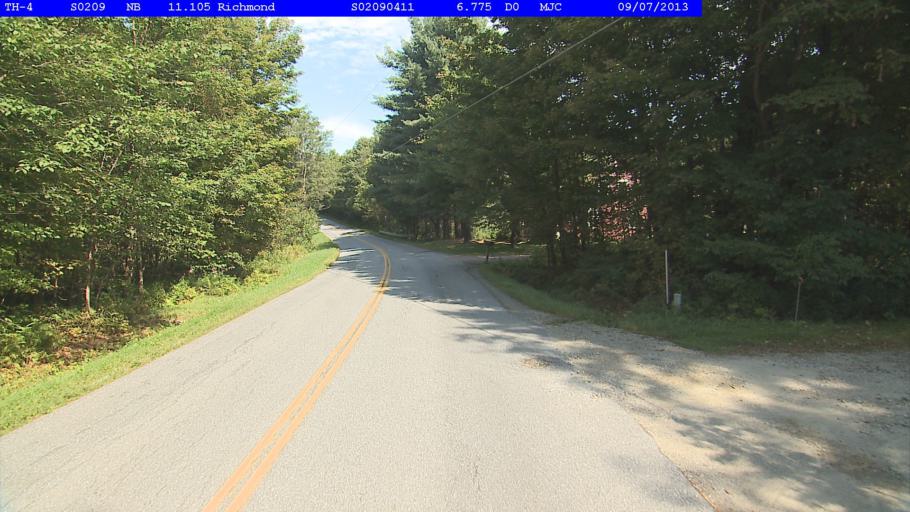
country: US
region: Vermont
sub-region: Chittenden County
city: Jericho
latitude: 44.4221
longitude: -72.9783
